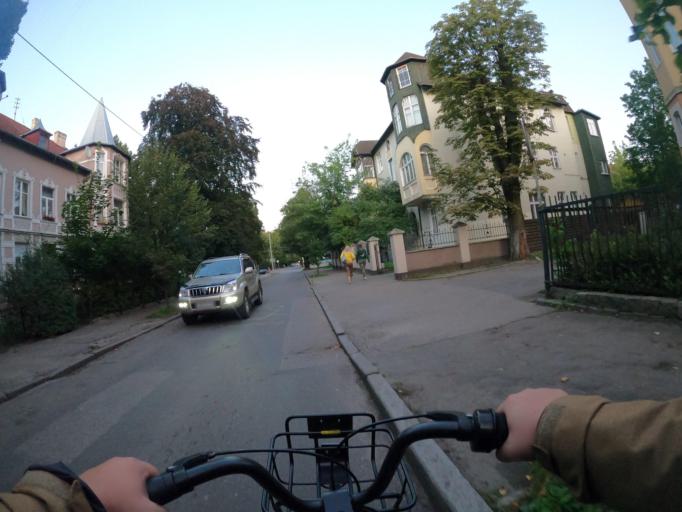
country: RU
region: Kaliningrad
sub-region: Gorod Kaliningrad
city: Kaliningrad
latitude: 54.7266
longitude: 20.4803
